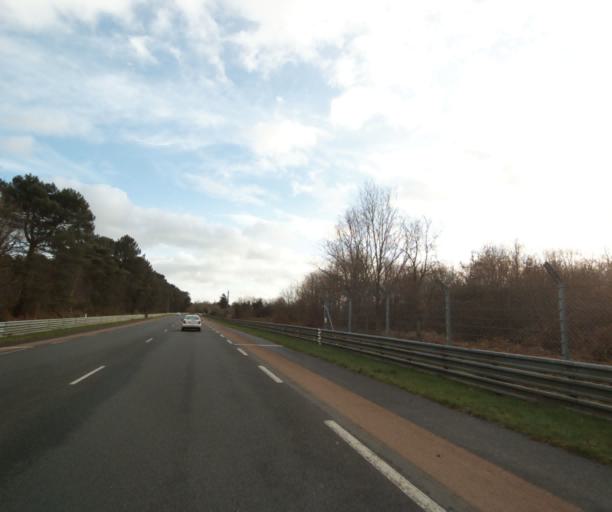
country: FR
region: Pays de la Loire
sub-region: Departement de la Sarthe
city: Arnage
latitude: 47.9289
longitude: 0.2119
